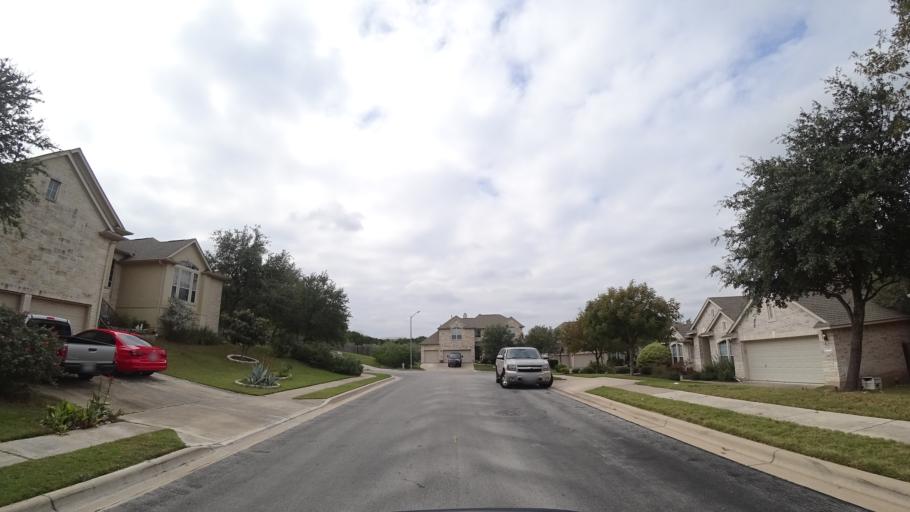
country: US
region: Texas
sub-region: Travis County
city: Shady Hollow
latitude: 30.2173
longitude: -97.8876
